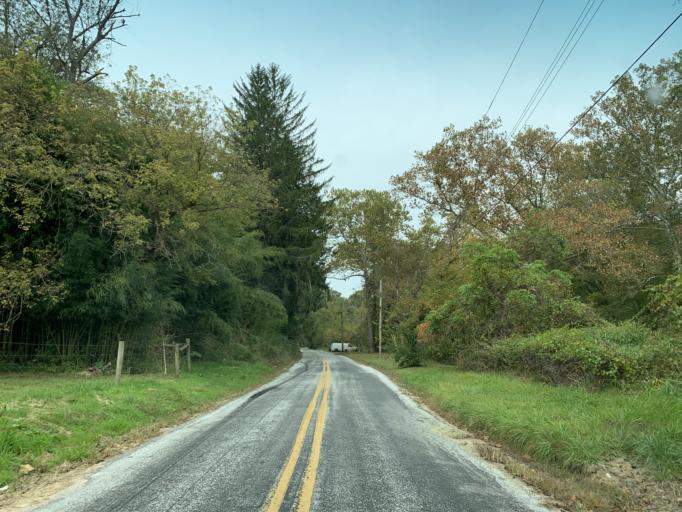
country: US
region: Pennsylvania
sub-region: York County
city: Susquehanna Trails
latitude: 39.7869
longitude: -76.4084
